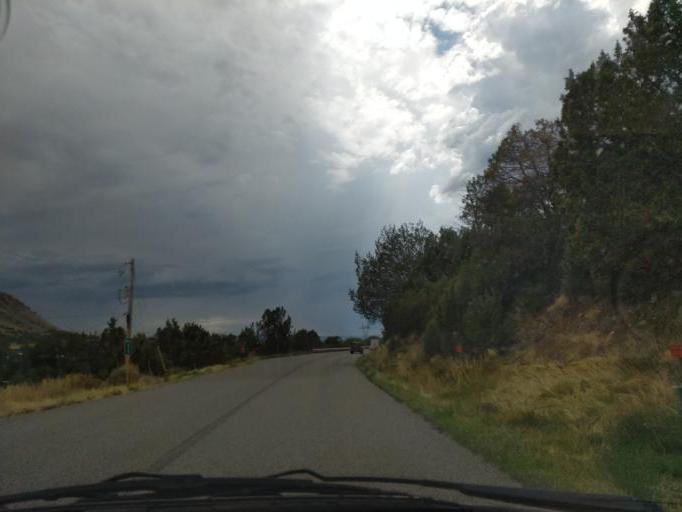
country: US
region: Colorado
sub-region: Delta County
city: Paonia
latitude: 38.8993
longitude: -107.5665
